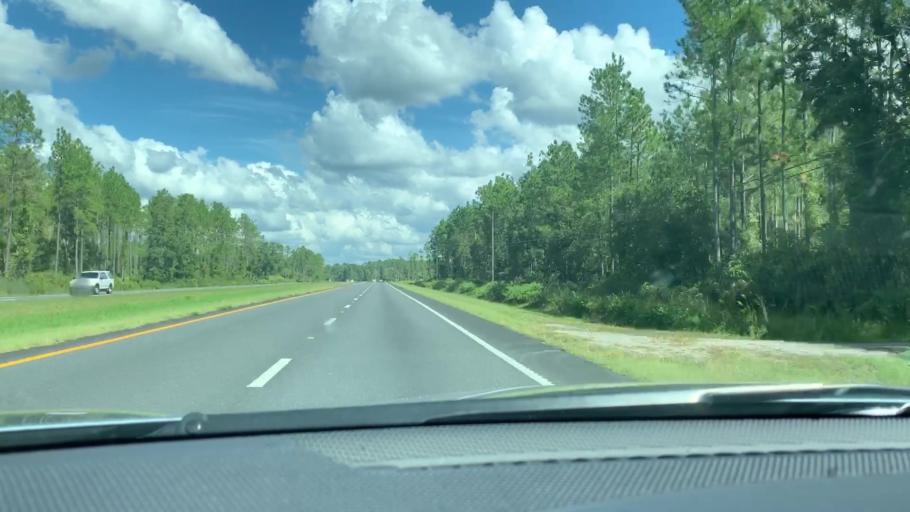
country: US
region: Florida
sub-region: Marion County
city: Citra
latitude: 29.4913
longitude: -82.1005
